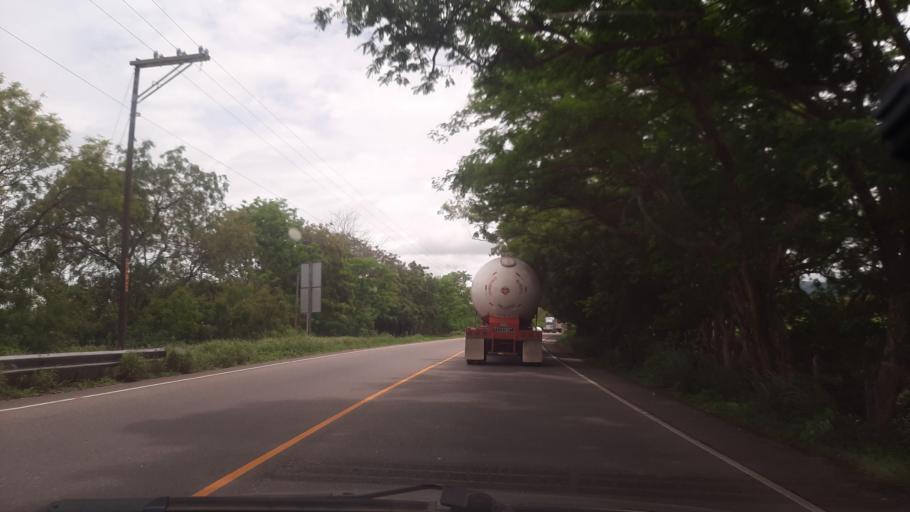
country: GT
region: Zacapa
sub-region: Municipio de Zacapa
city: Gualan
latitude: 15.0859
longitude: -89.4586
